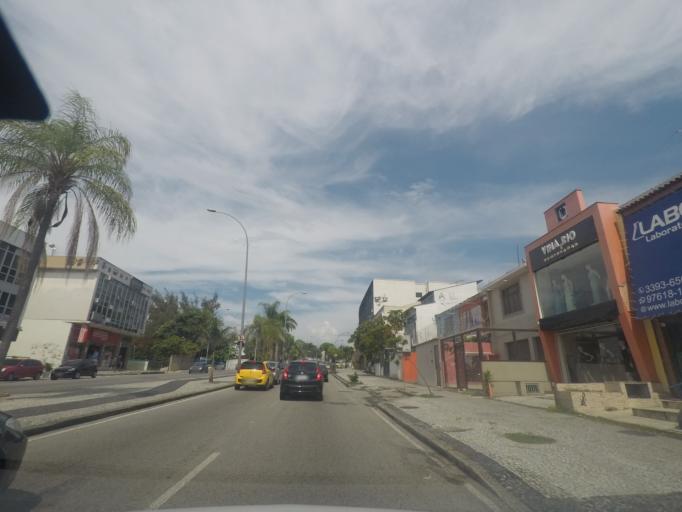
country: BR
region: Rio de Janeiro
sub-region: Rio De Janeiro
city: Rio de Janeiro
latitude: -22.8044
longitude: -43.2054
